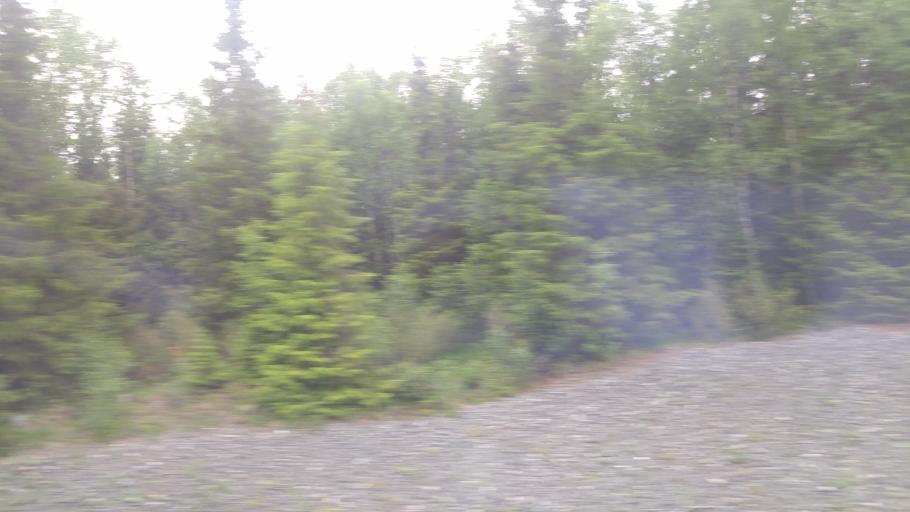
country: SE
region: Jaemtland
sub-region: Are Kommun
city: Are
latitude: 63.3723
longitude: 12.7243
